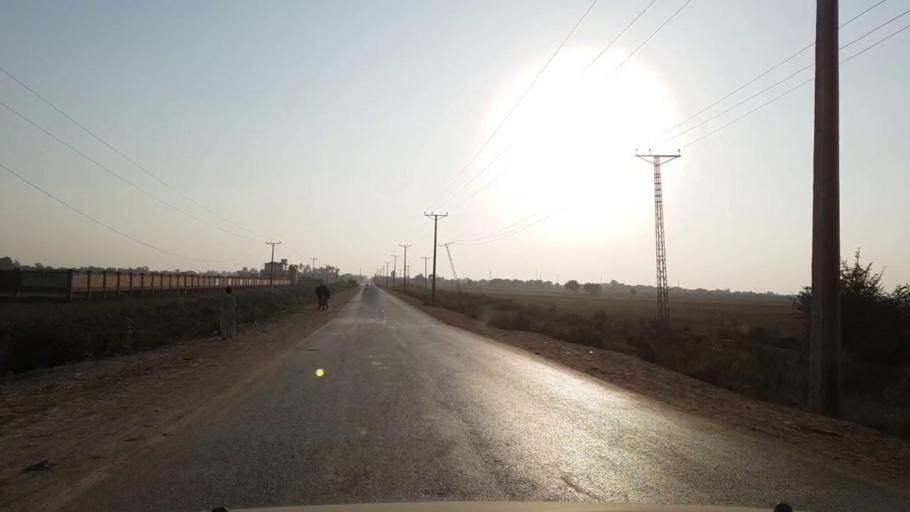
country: PK
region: Sindh
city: Daro Mehar
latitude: 24.6140
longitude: 68.0893
